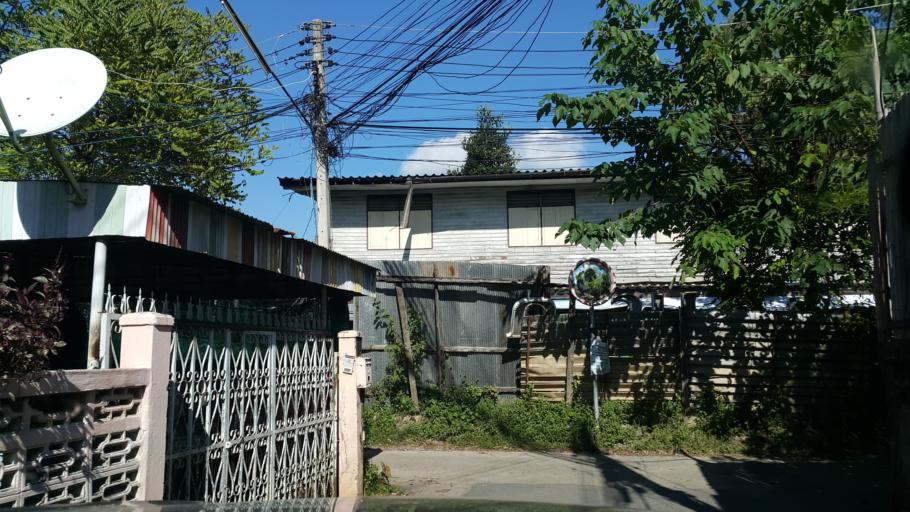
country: TH
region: Chiang Mai
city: Chiang Mai
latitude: 18.7630
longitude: 99.0001
